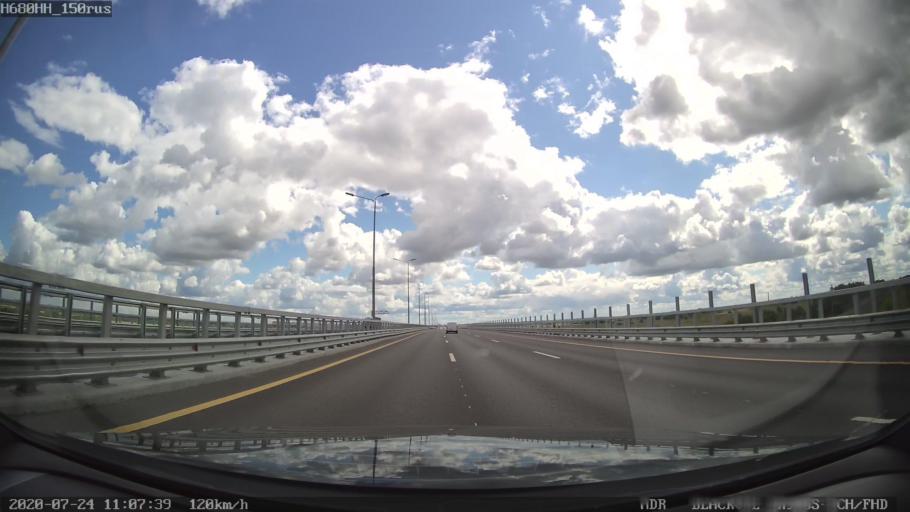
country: RU
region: St.-Petersburg
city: Pushkin
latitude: 59.7555
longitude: 30.4128
